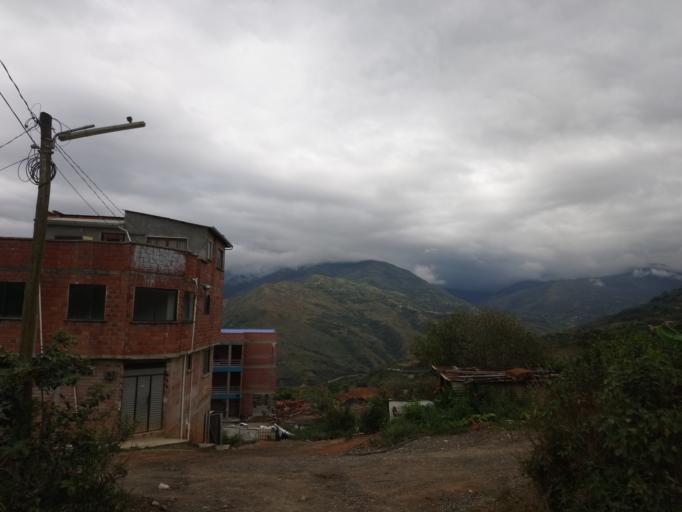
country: BO
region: La Paz
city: Coripata
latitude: -16.2724
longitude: -67.6365
